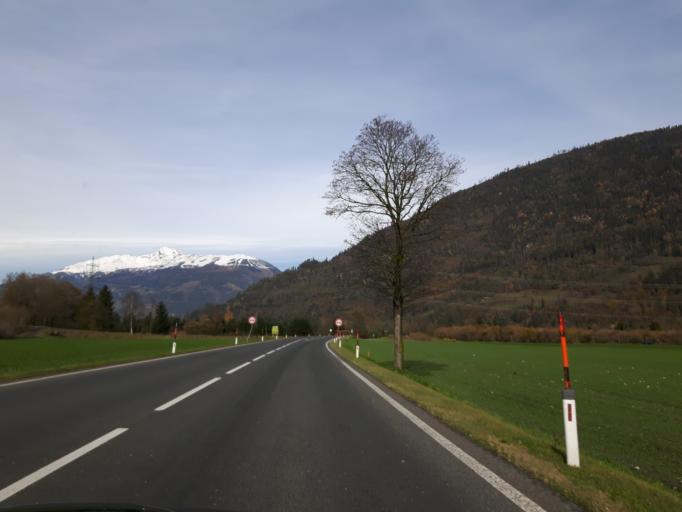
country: AT
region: Tyrol
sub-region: Politischer Bezirk Lienz
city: Nikolsdorf
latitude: 46.7896
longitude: 12.8772
